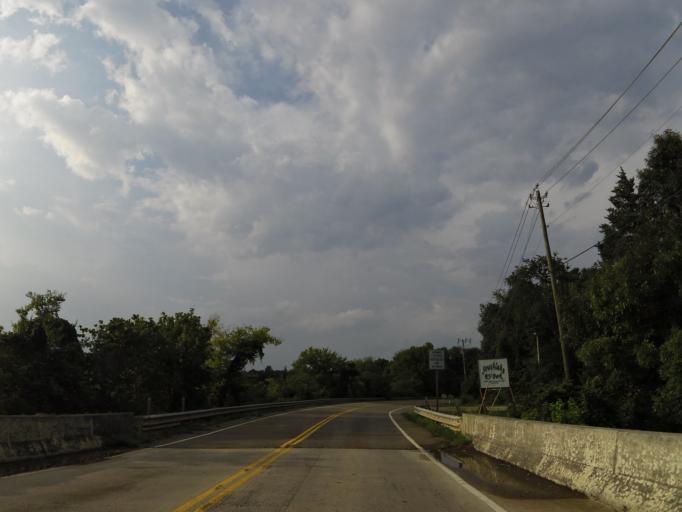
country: US
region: Tennessee
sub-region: Blount County
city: Eagleton Village
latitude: 35.8718
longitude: -83.9436
